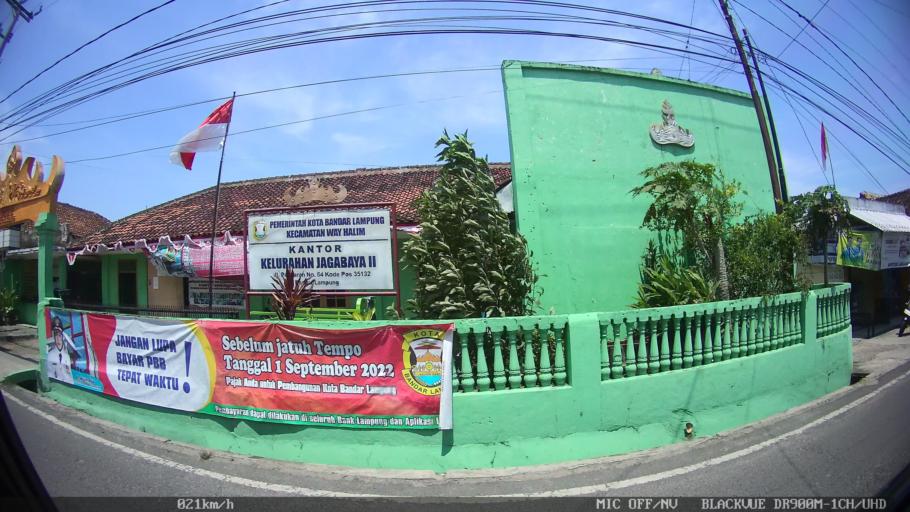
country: ID
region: Lampung
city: Kedaton
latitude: -5.3985
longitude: 105.2647
